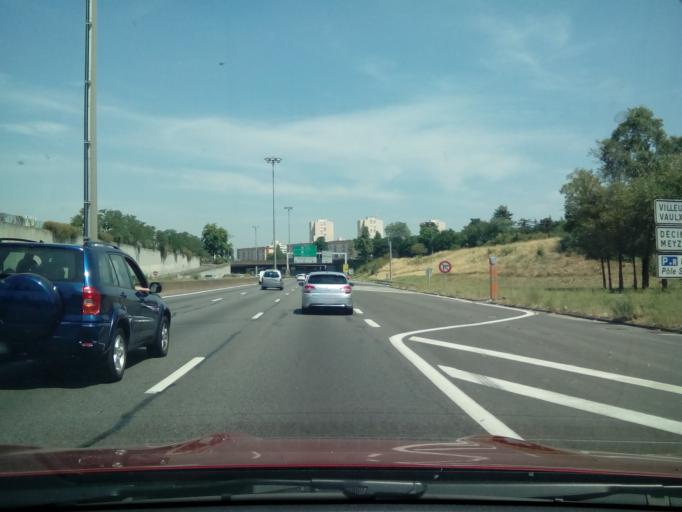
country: FR
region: Rhone-Alpes
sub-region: Departement du Rhone
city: Vaulx-en-Velin
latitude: 45.7585
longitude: 4.9093
